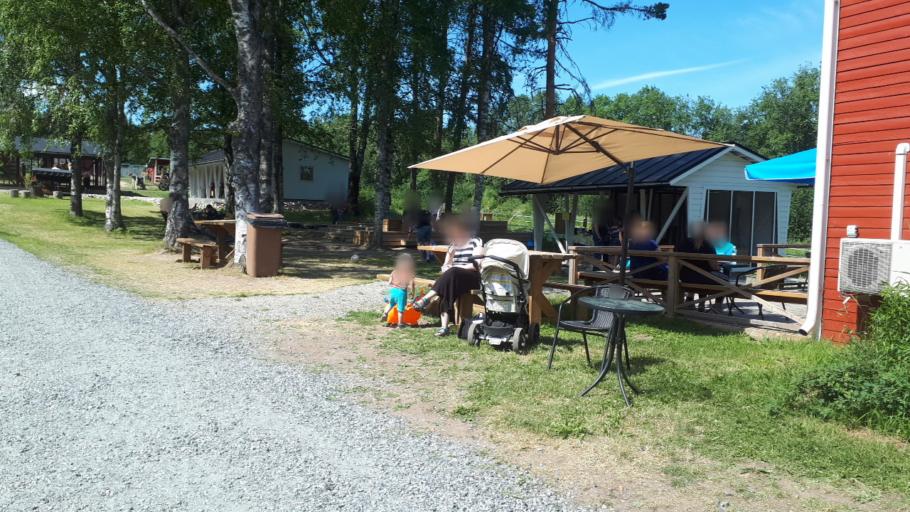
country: FI
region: Northern Savo
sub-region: Kuopio
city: Kuopio
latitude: 62.7515
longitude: 27.5533
